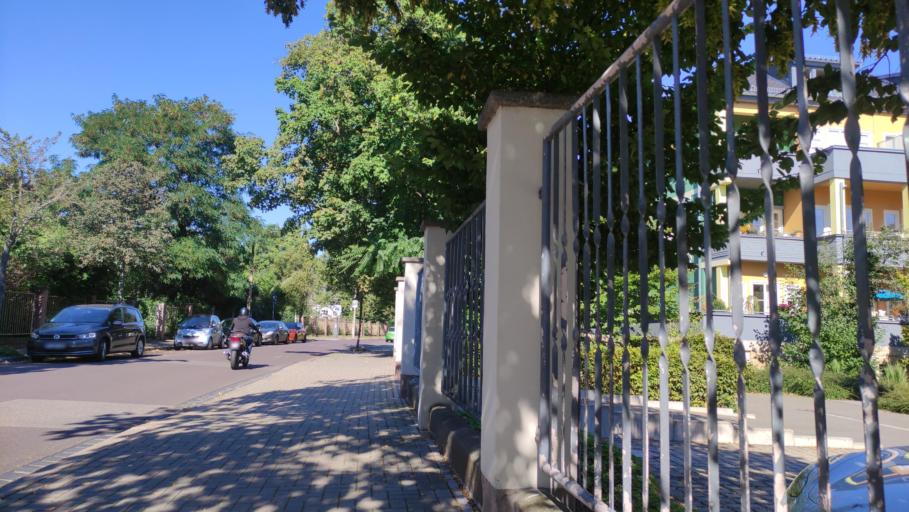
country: DE
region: Thuringia
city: Erfurt
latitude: 50.9700
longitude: 11.0249
